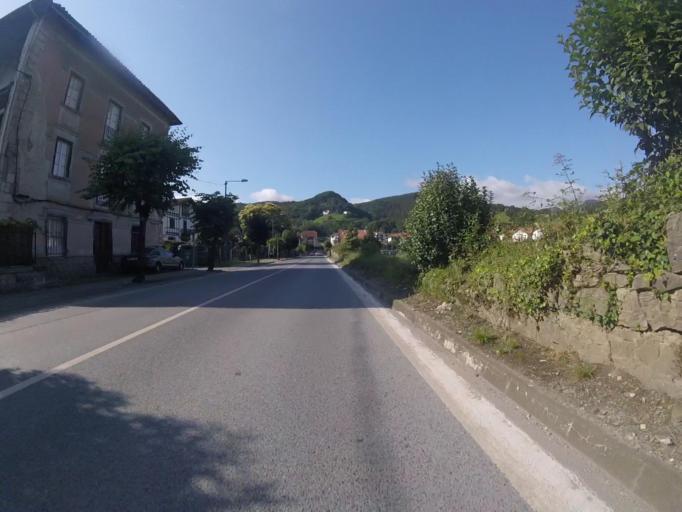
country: ES
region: Navarre
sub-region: Provincia de Navarra
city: Bera
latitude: 43.2775
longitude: -1.6886
